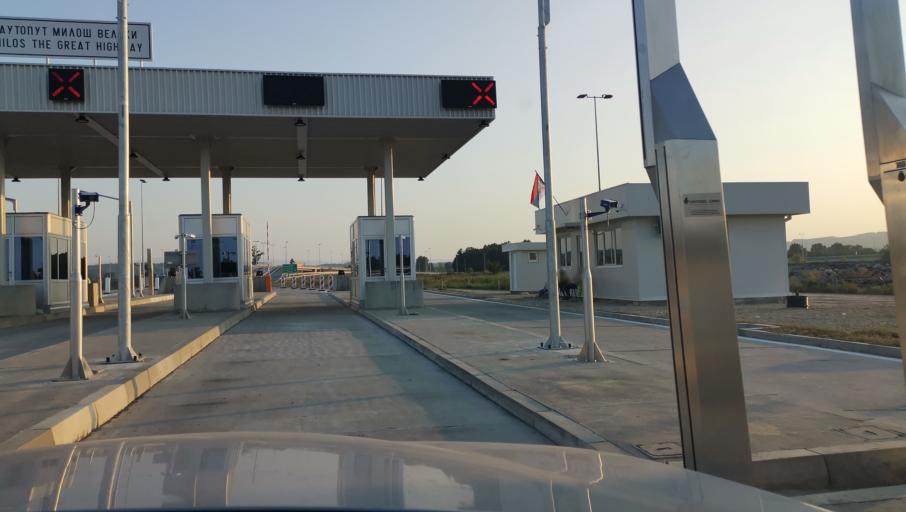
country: RS
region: Central Serbia
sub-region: Kolubarski Okrug
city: Lajkovac
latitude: 44.3601
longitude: 20.1310
